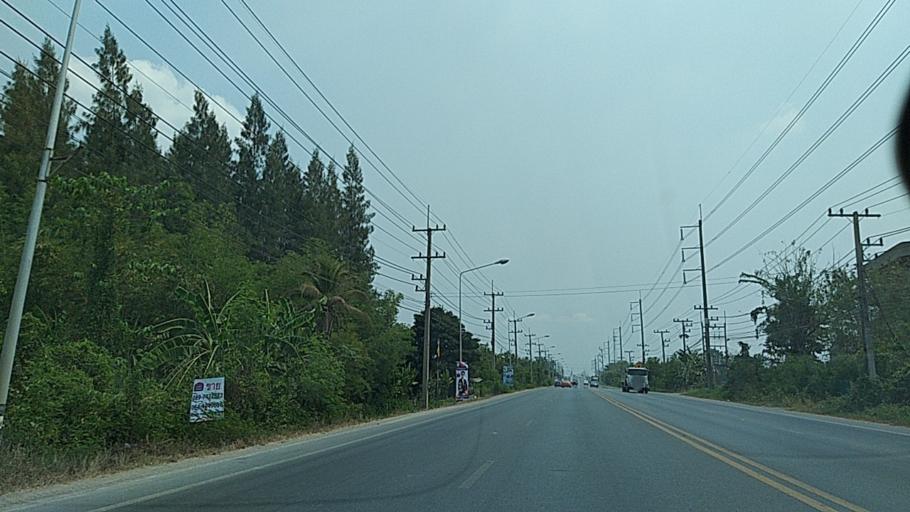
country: TH
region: Bangkok
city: Nong Chok
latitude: 13.9602
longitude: 100.8865
